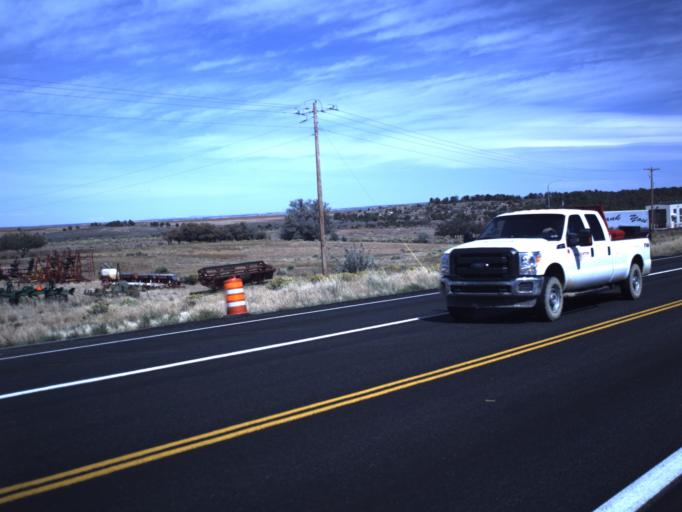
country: US
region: Utah
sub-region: San Juan County
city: Monticello
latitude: 37.8727
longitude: -109.3102
